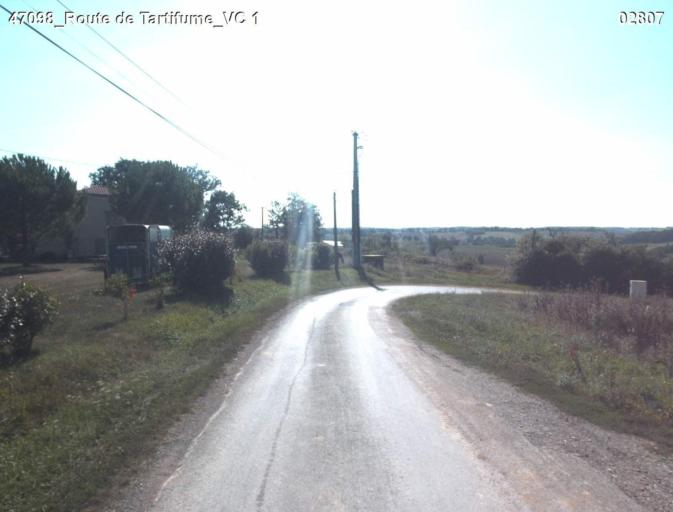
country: FR
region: Aquitaine
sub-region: Departement du Lot-et-Garonne
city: Nerac
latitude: 44.0904
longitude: 0.4092
